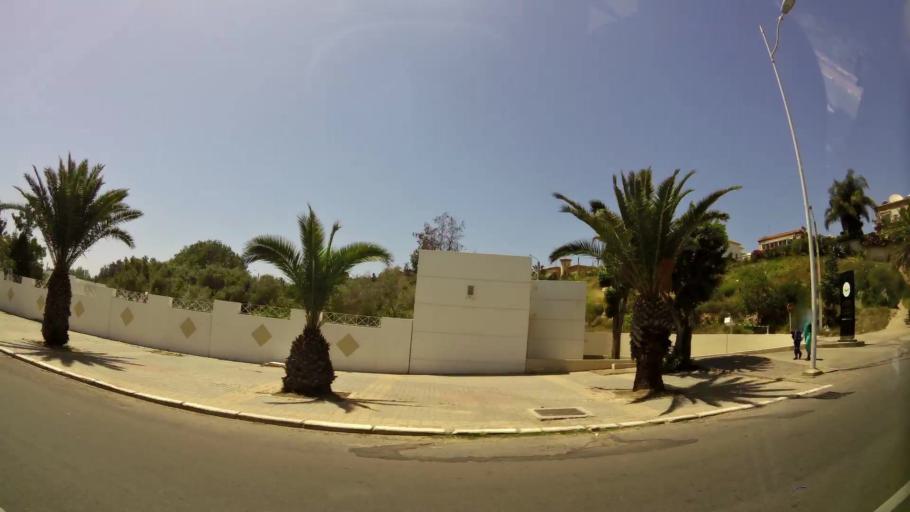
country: MA
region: Souss-Massa-Draa
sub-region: Agadir-Ida-ou-Tnan
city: Agadir
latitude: 30.4286
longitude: -9.5926
